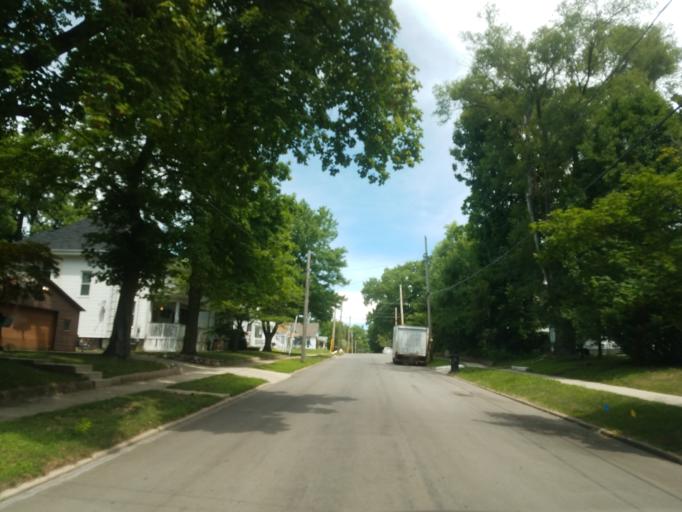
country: US
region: Illinois
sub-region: McLean County
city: Bloomington
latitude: 40.4713
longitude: -88.9856
